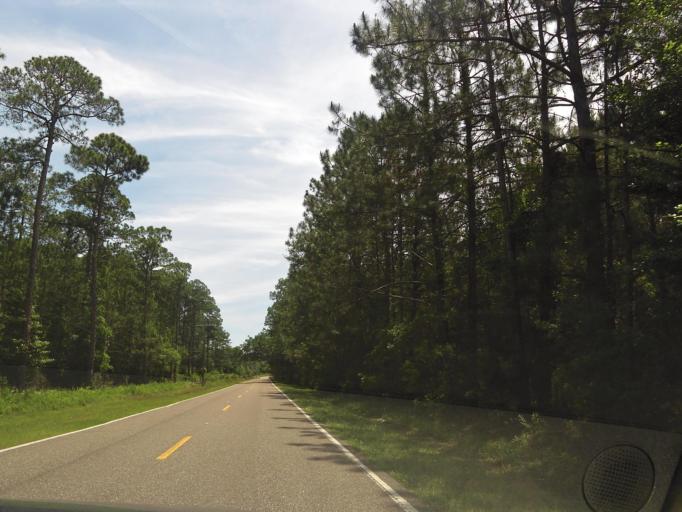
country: US
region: Florida
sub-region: Duval County
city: Atlantic Beach
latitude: 30.4590
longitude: -81.5250
